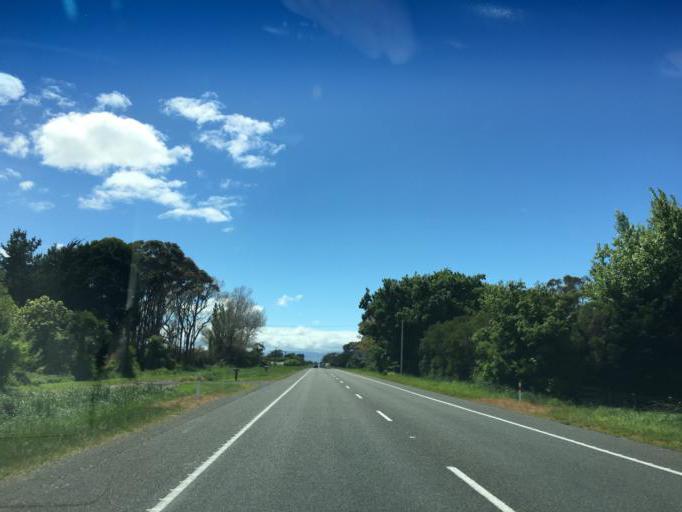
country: NZ
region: Manawatu-Wanganui
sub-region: Palmerston North City
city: Palmerston North
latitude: -40.3997
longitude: 175.5071
